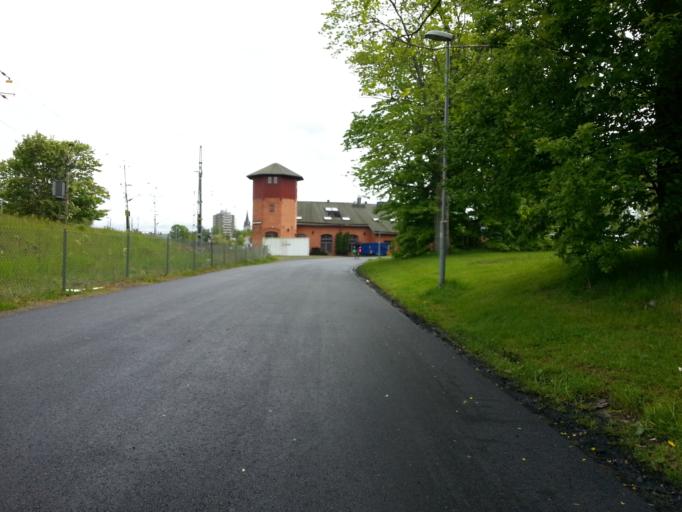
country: SE
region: Joenkoeping
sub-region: Jonkopings Kommun
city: Jonkoping
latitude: 57.7886
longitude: 14.1502
